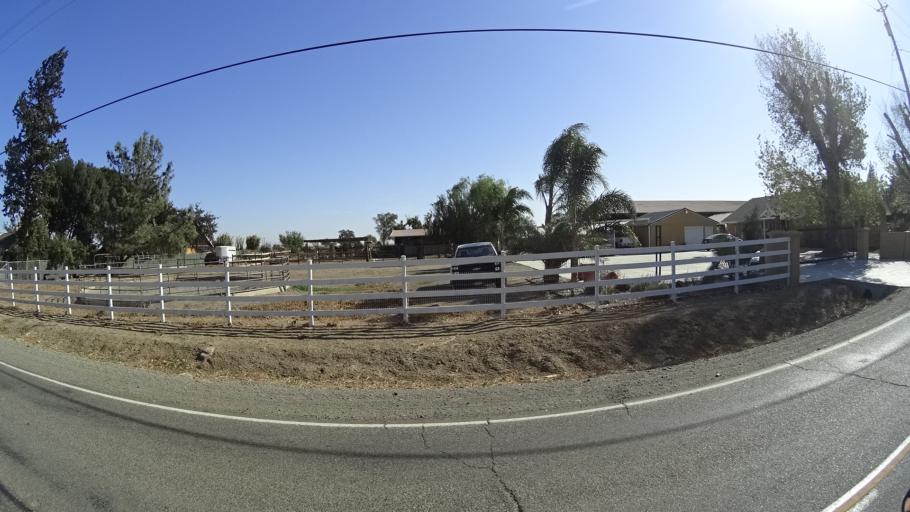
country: US
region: California
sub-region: Yolo County
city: Cottonwood
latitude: 38.6595
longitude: -121.9710
